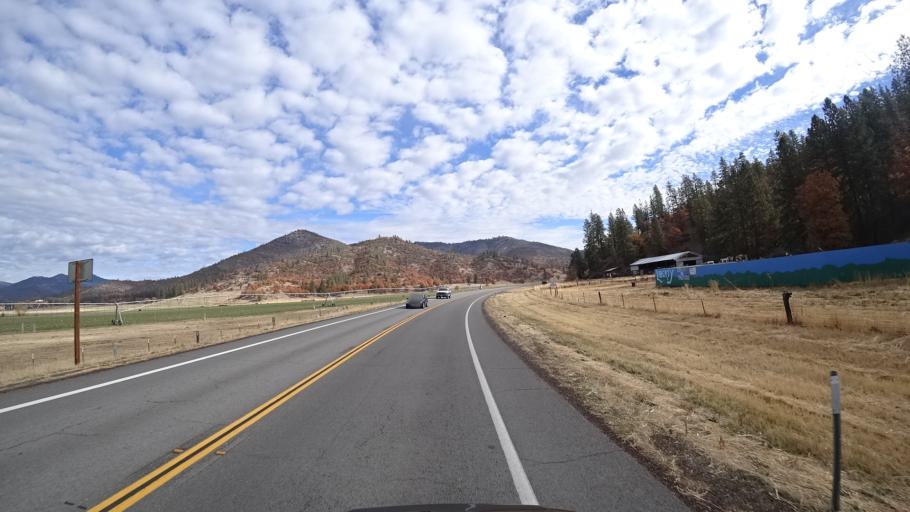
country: US
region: California
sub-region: Siskiyou County
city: Yreka
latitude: 41.6252
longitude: -122.8258
